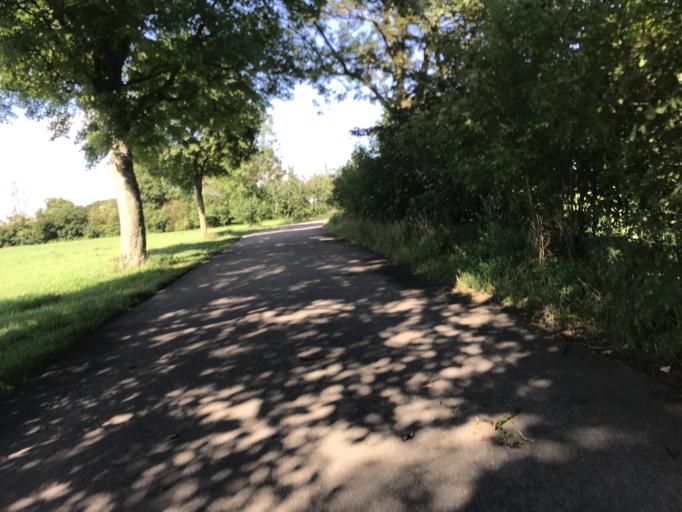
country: DE
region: Baden-Wuerttemberg
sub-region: Tuebingen Region
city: Langenau
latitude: 48.4785
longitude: 10.1279
